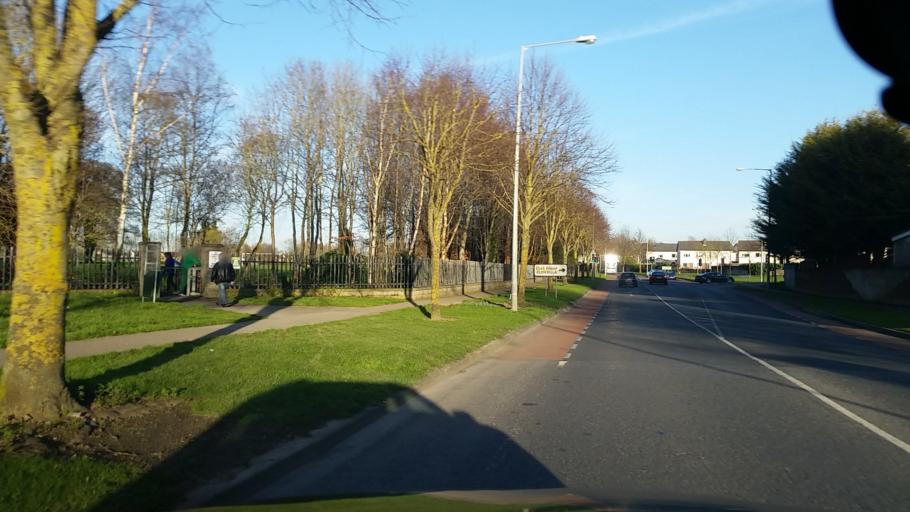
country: IE
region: Leinster
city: Hartstown
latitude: 53.3910
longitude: -6.4147
